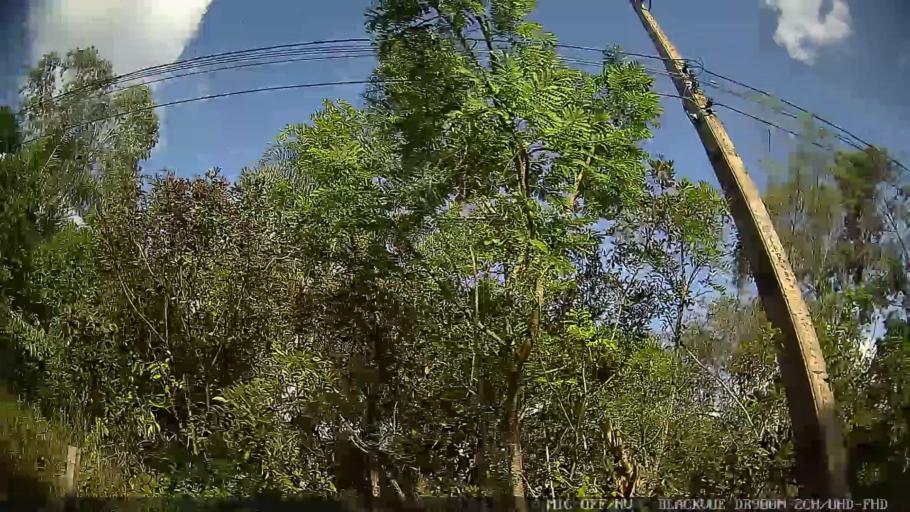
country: BR
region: Sao Paulo
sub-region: Braganca Paulista
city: Braganca Paulista
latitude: -22.9603
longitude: -46.5147
